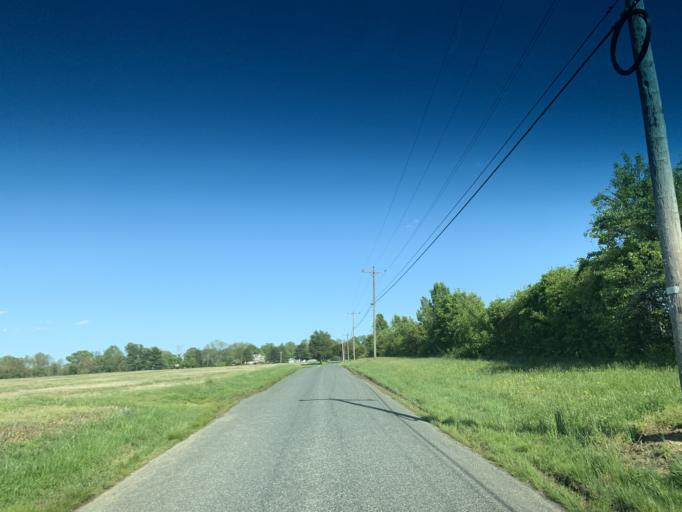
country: US
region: Maryland
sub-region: Harford County
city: Aberdeen
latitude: 39.5014
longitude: -76.1421
